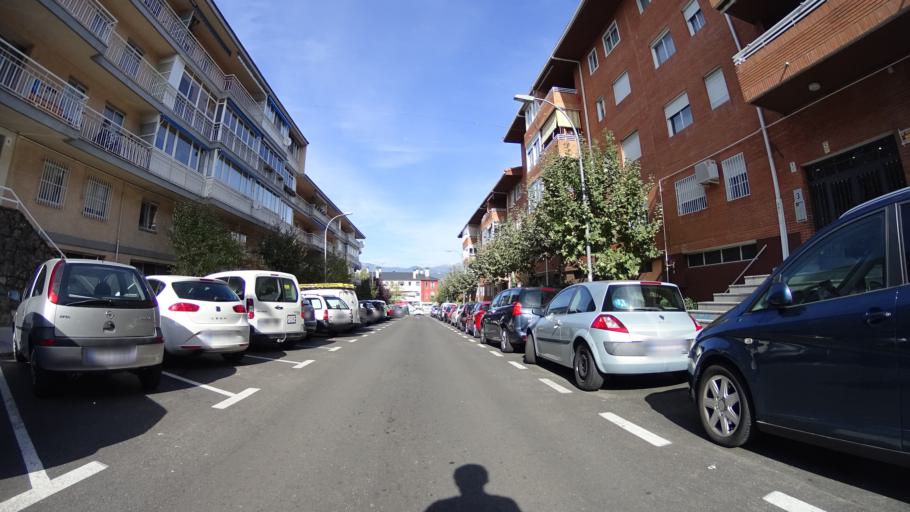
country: ES
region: Madrid
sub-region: Provincia de Madrid
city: Collado-Villalba
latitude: 40.6226
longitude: -4.0114
